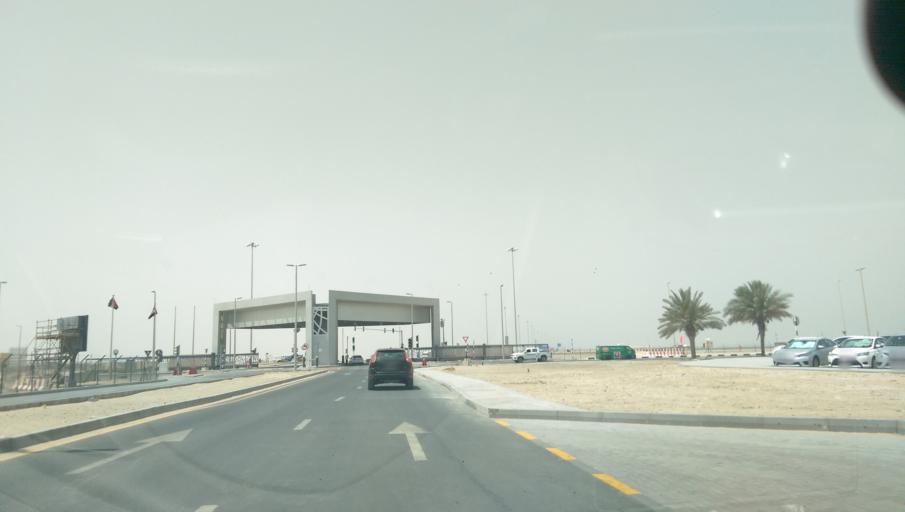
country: AE
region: Abu Dhabi
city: Abu Dhabi
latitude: 24.7806
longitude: 54.7296
